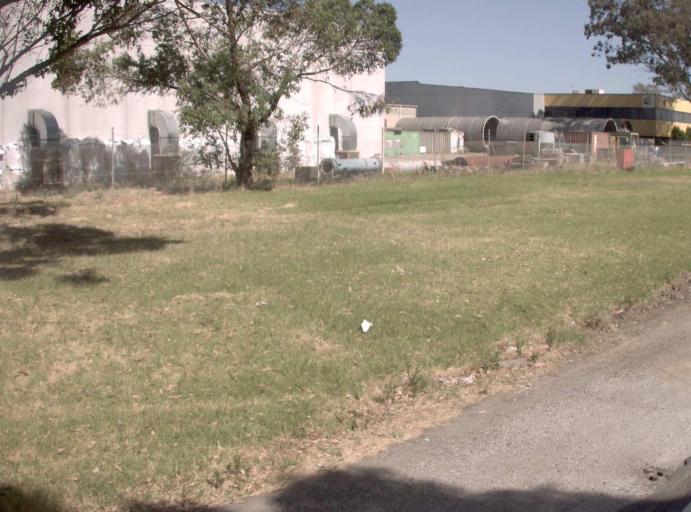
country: AU
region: Victoria
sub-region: Casey
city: Hampton Park
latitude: -38.0324
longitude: 145.2119
